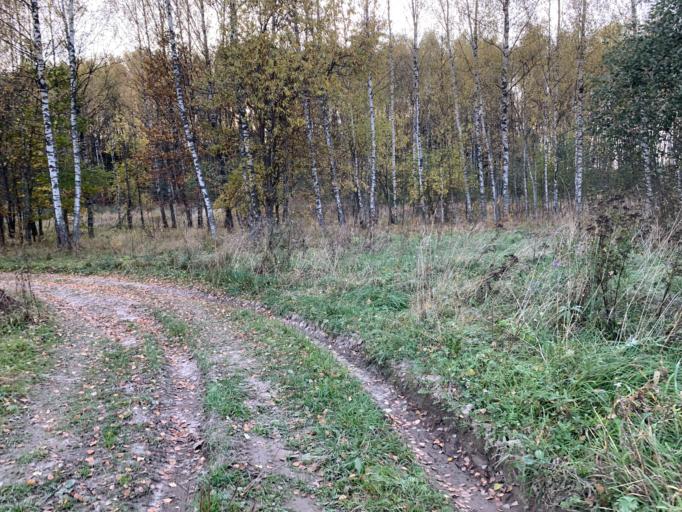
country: RU
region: Jaroslavl
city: Porech'ye-Rybnoye
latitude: 56.9869
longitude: 39.3804
